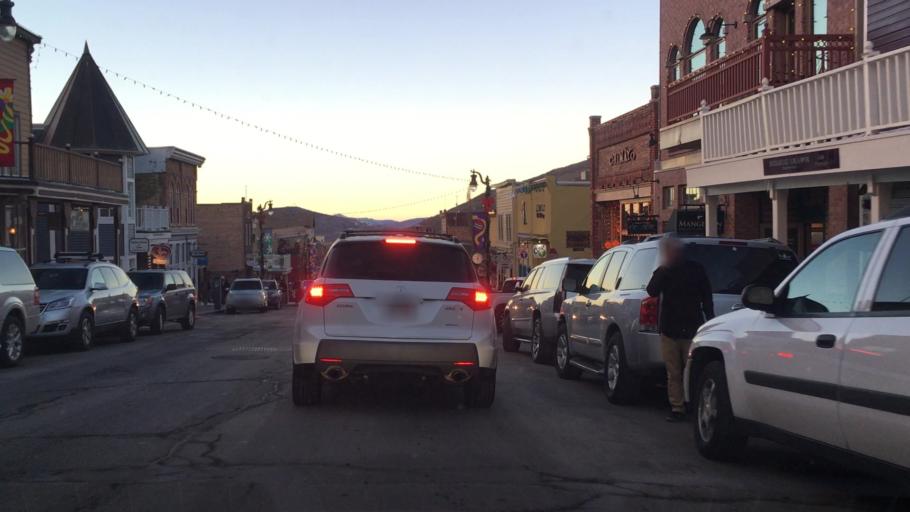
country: US
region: Utah
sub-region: Summit County
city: Park City
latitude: 40.6428
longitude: -111.4954
